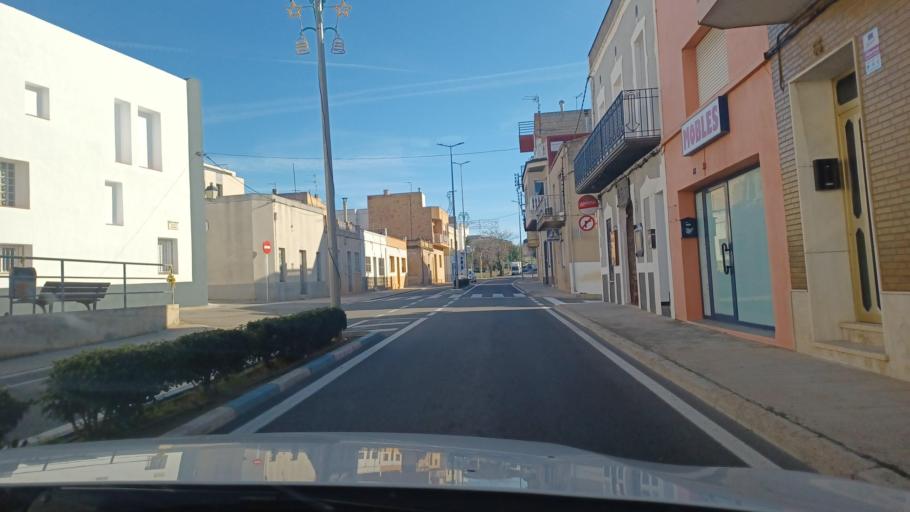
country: ES
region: Catalonia
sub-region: Provincia de Tarragona
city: Masdenverge
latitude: 40.7139
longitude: 0.5316
